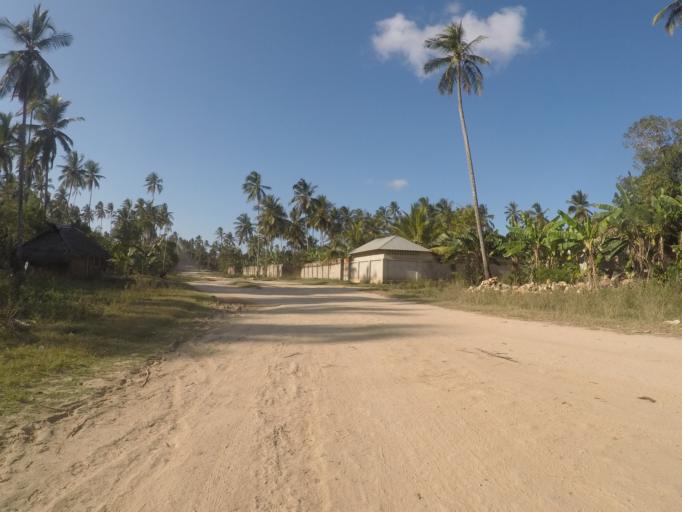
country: TZ
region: Zanzibar Central/South
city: Koani
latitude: -6.1663
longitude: 39.2866
